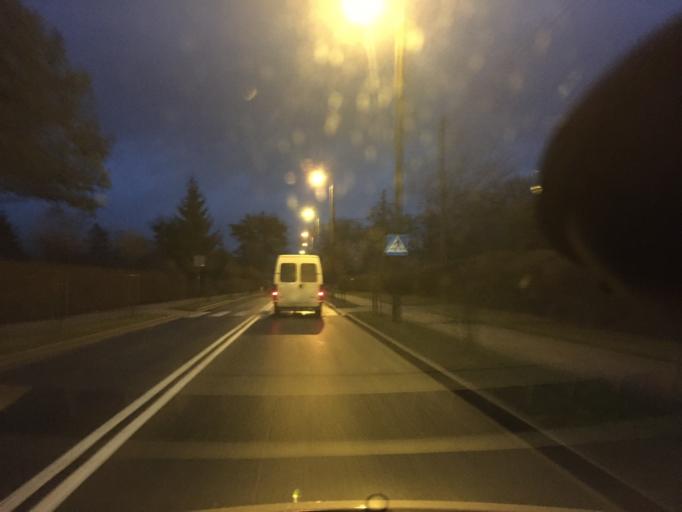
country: PL
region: Kujawsko-Pomorskie
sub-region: Powiat golubsko-dobrzynski
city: Kowalewo Pomorskie
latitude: 53.1515
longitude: 18.8922
